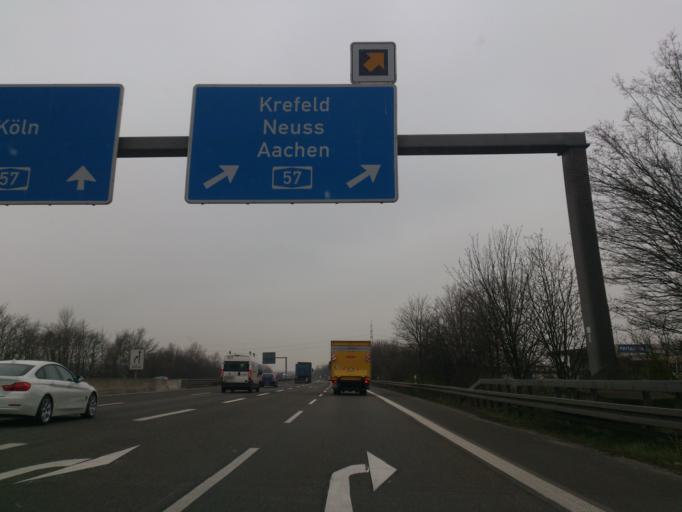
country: DE
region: North Rhine-Westphalia
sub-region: Regierungsbezirk Dusseldorf
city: Dusseldorf
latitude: 51.1603
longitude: 6.7619
